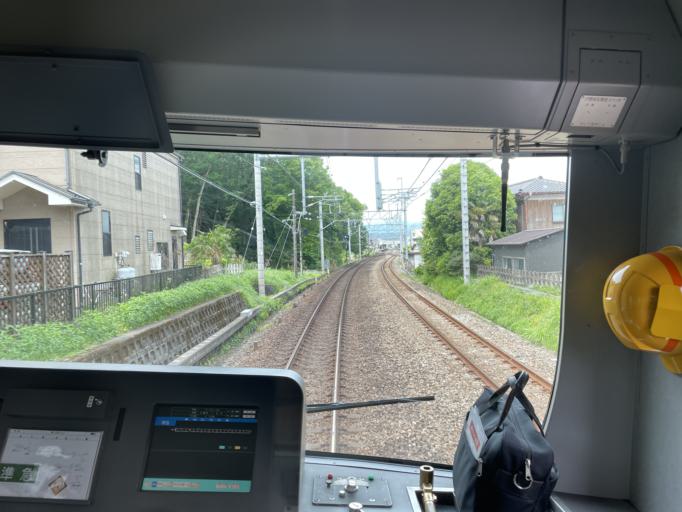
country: JP
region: Saitama
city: Hanno
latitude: 35.8379
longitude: 139.3652
